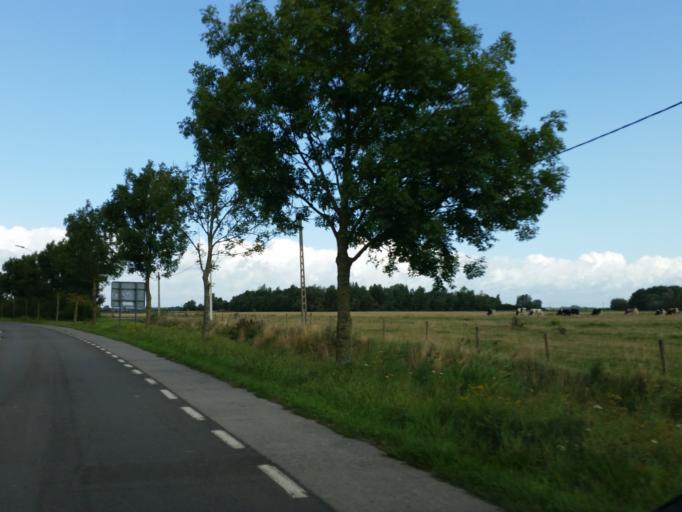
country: BE
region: Flanders
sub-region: Provincie West-Vlaanderen
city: De Haan
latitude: 51.2317
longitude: 3.0396
